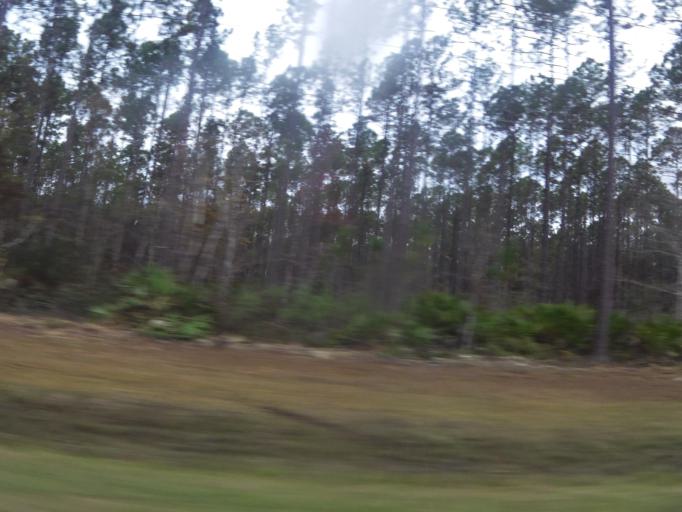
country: US
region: Georgia
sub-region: Charlton County
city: Folkston
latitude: 30.8894
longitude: -82.0616
